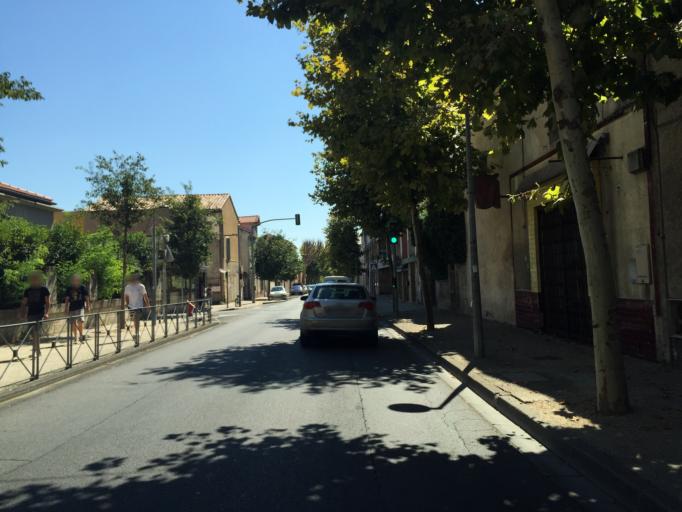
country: FR
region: Provence-Alpes-Cote d'Azur
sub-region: Departement du Vaucluse
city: Carpentras
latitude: 44.0495
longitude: 5.0478
